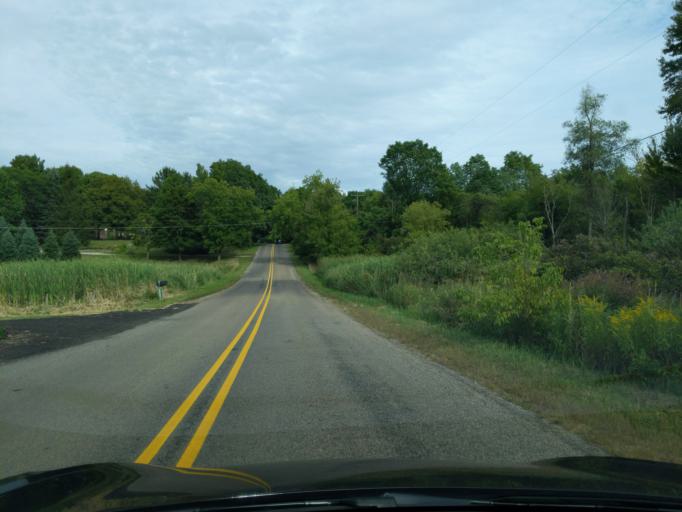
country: US
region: Michigan
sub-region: Eaton County
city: Dimondale
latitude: 42.6691
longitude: -84.6354
